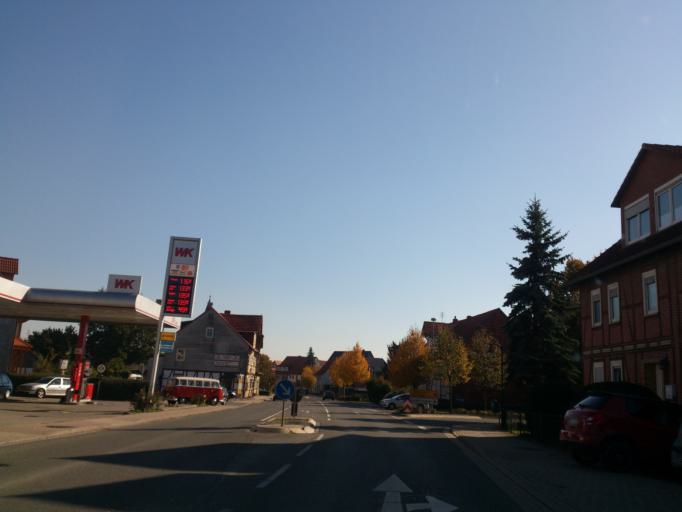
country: DE
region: Hesse
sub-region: Regierungsbezirk Kassel
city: Calden
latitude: 51.4101
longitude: 9.3966
